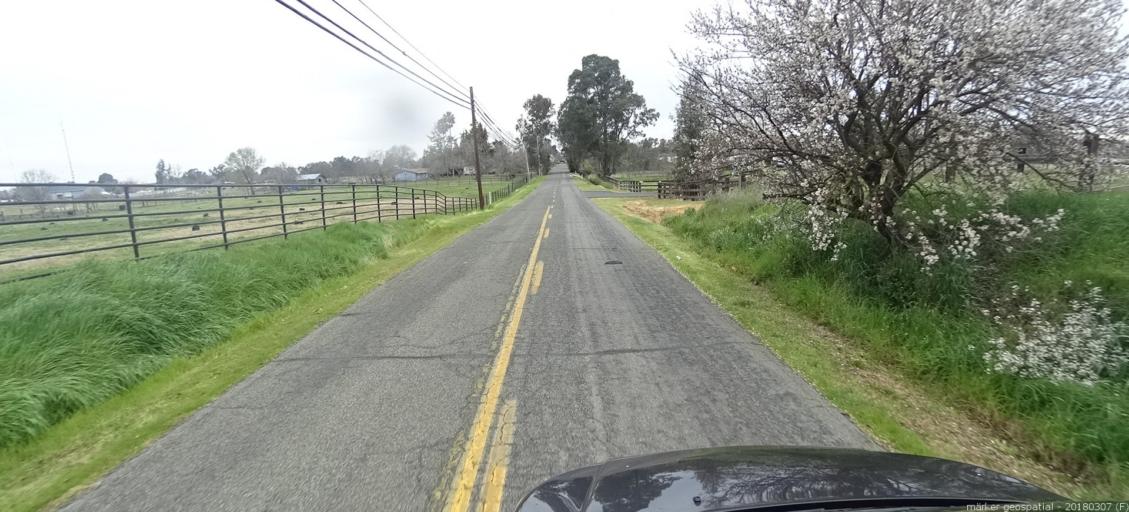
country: US
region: California
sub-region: Sacramento County
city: Elverta
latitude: 38.6992
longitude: -121.4661
